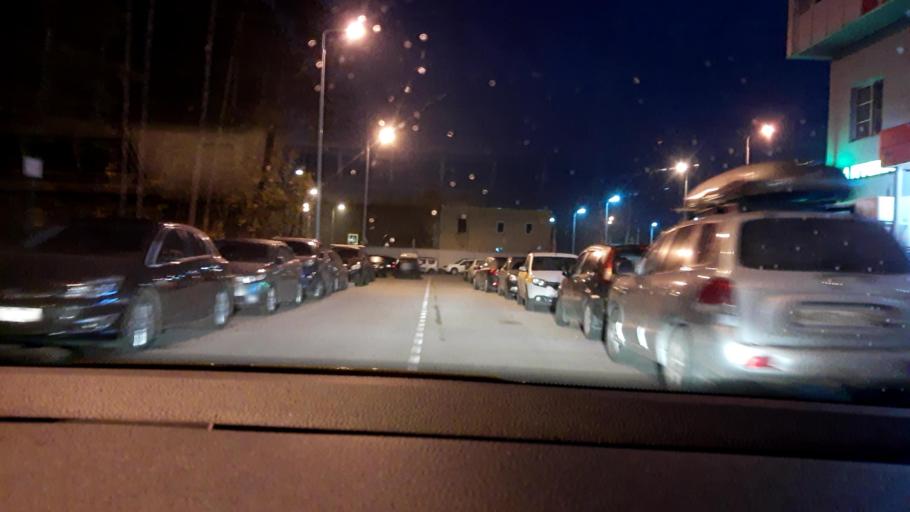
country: RU
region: Moscow
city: Vostochnyy
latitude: 55.8235
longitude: 37.8877
